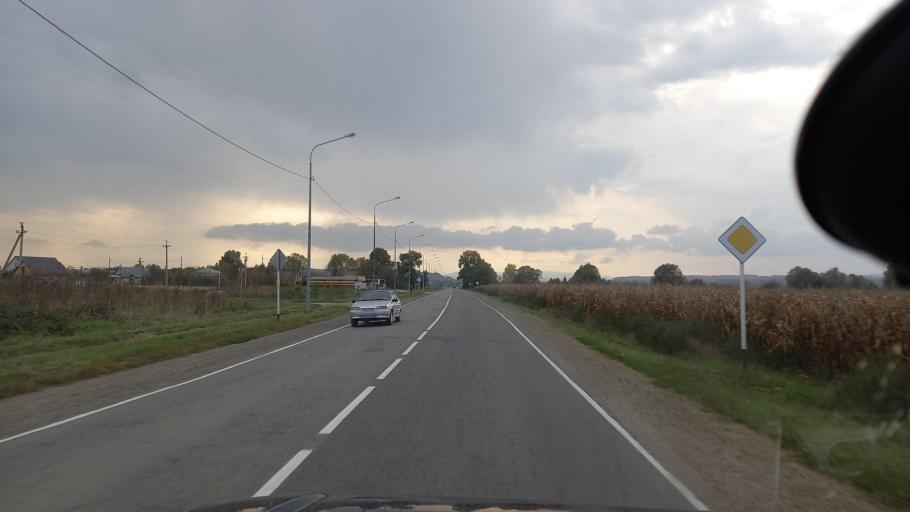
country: RU
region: Krasnodarskiy
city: Mostovskoy
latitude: 44.3981
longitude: 40.7743
